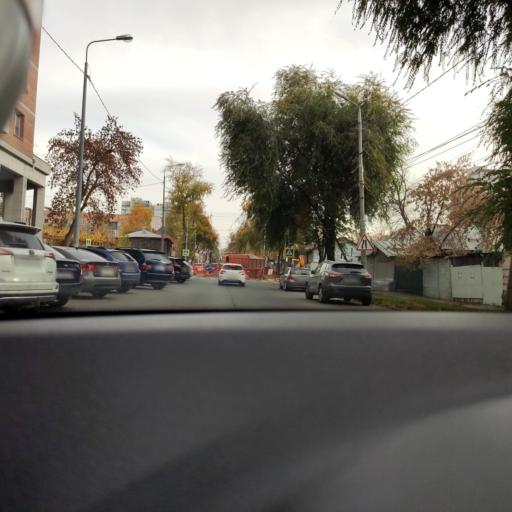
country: RU
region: Samara
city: Samara
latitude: 53.2012
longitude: 50.1231
